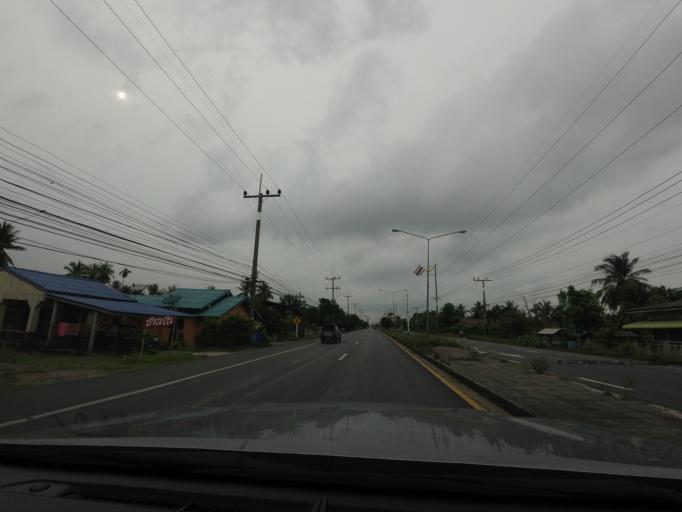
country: TH
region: Songkhla
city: Sathing Phra
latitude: 7.3790
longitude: 100.4738
